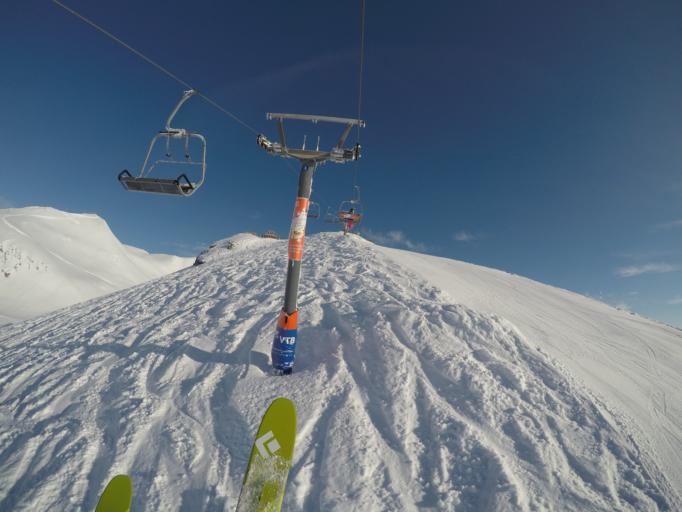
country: GE
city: Gudauri
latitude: 42.4959
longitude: 44.5066
